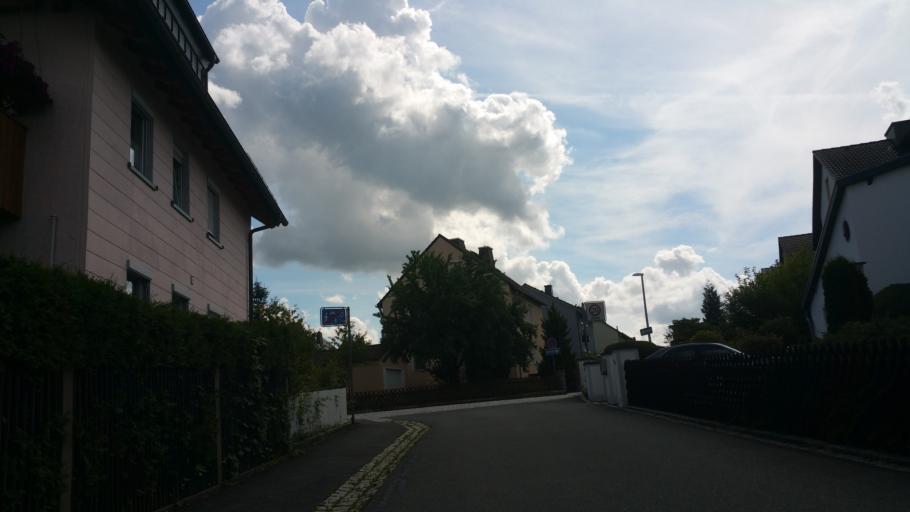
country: DE
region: Bavaria
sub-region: Upper Franconia
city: Oberkotzau
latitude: 50.2640
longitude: 11.9287
